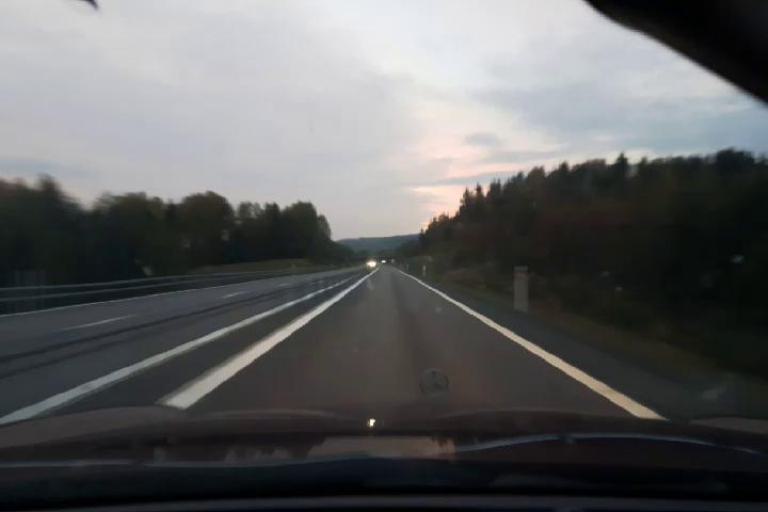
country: SE
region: Vaesternorrland
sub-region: Kramfors Kommun
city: Nordingra
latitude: 62.9340
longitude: 18.0949
